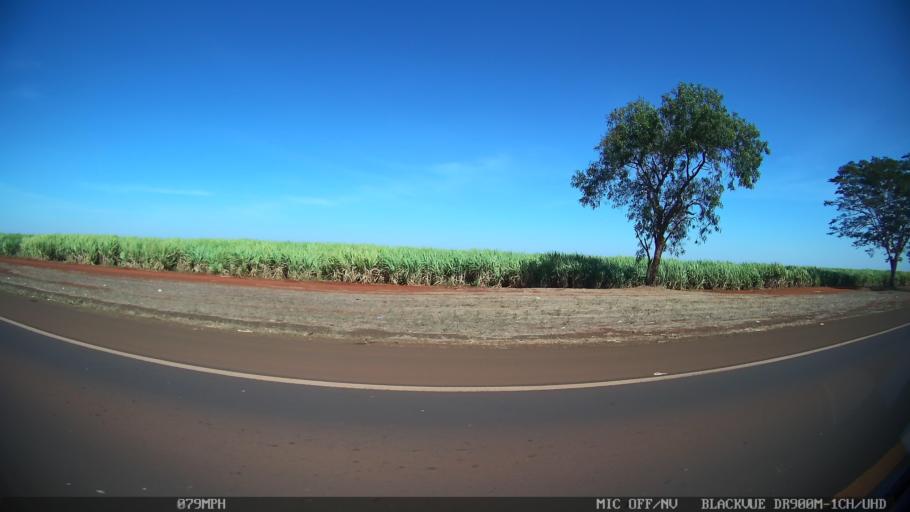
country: BR
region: Sao Paulo
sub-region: Guaira
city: Guaira
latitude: -20.4443
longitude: -48.2809
